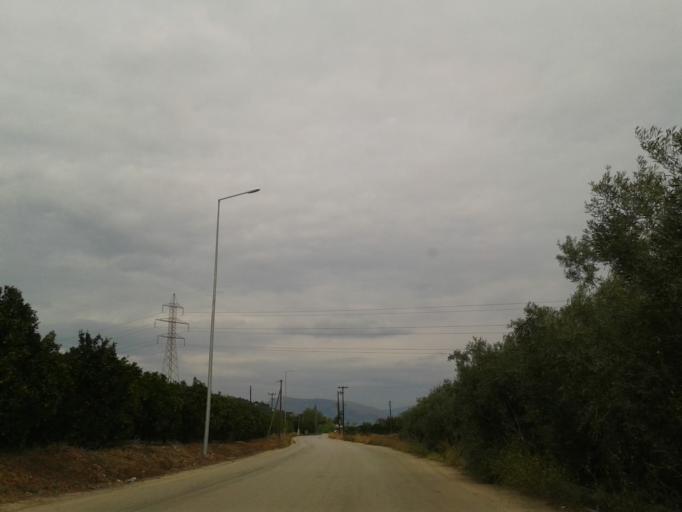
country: GR
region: Peloponnese
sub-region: Nomos Argolidos
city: Argos
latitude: 37.6069
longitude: 22.6993
